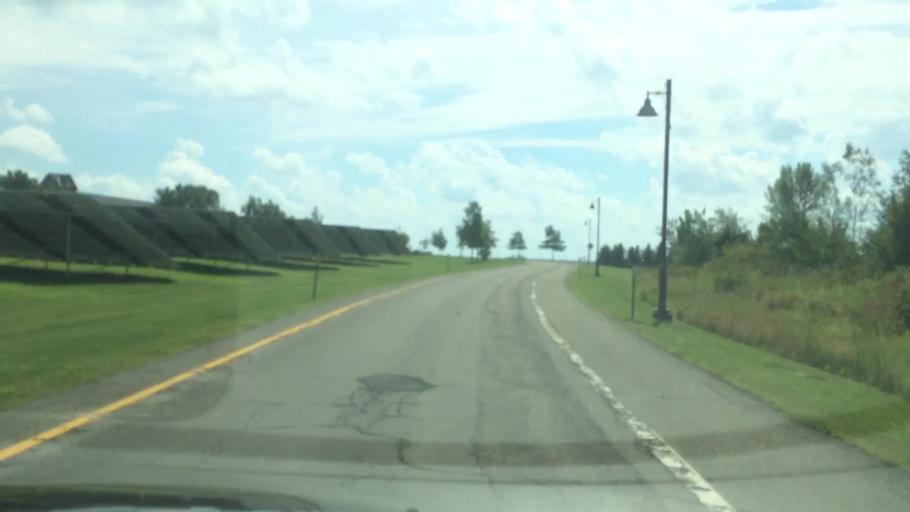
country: US
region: New York
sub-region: Chautauqua County
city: Lakewood
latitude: 42.1359
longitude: -79.3502
